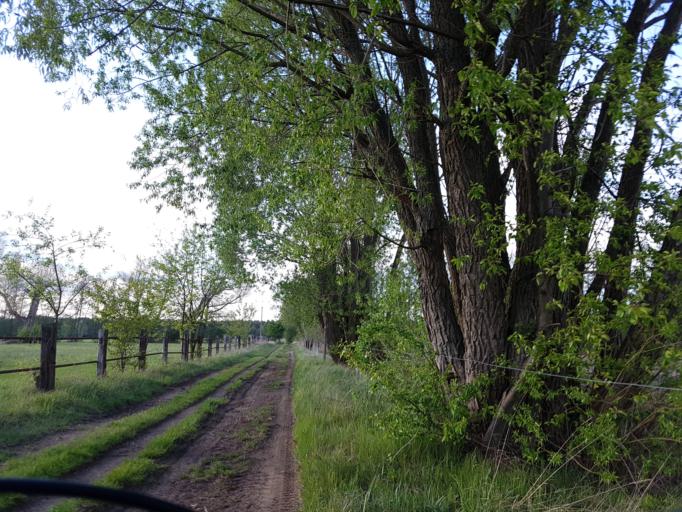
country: DE
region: Brandenburg
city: Schilda
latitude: 51.5795
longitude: 13.3656
